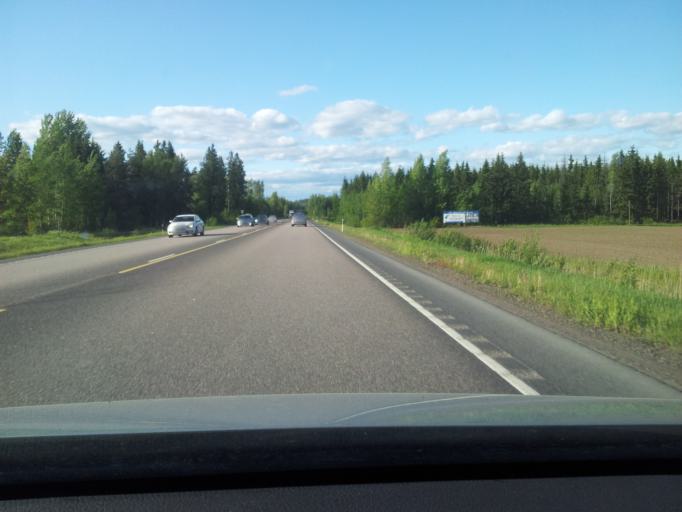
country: FI
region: Kymenlaakso
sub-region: Kouvola
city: Elimaeki
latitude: 60.8378
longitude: 26.5409
